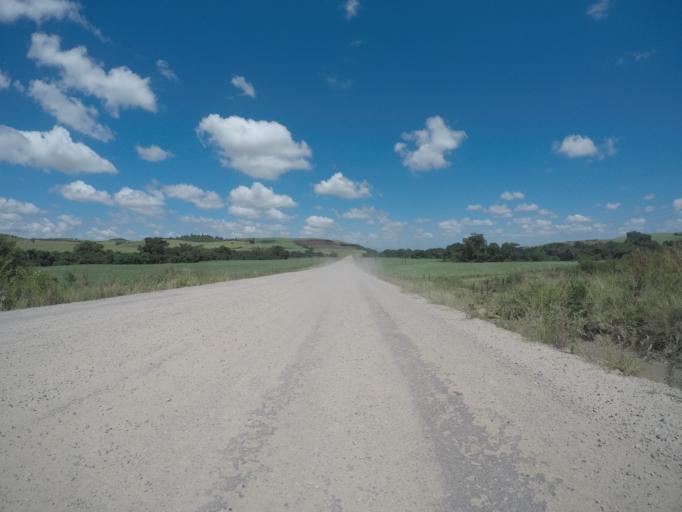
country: ZA
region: KwaZulu-Natal
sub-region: uThungulu District Municipality
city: Empangeni
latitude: -28.6416
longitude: 31.7649
